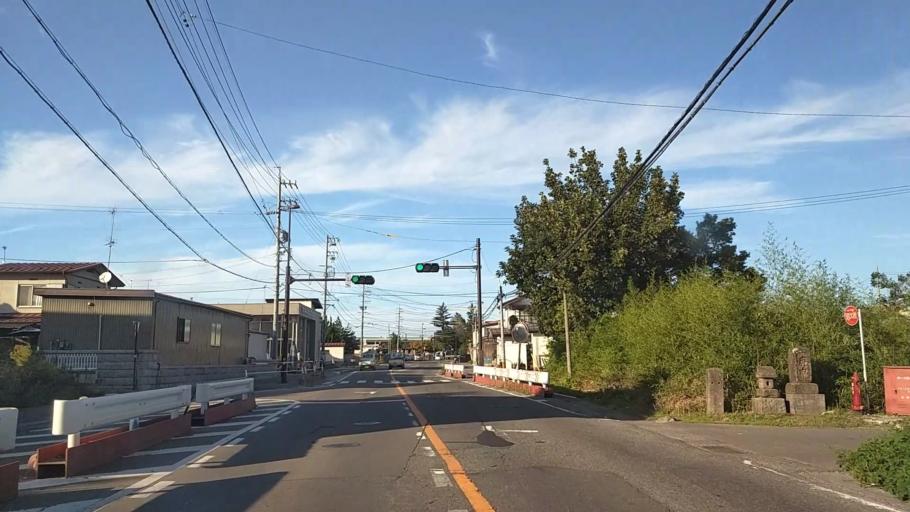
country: JP
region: Nagano
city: Nagano-shi
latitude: 36.5898
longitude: 138.1989
